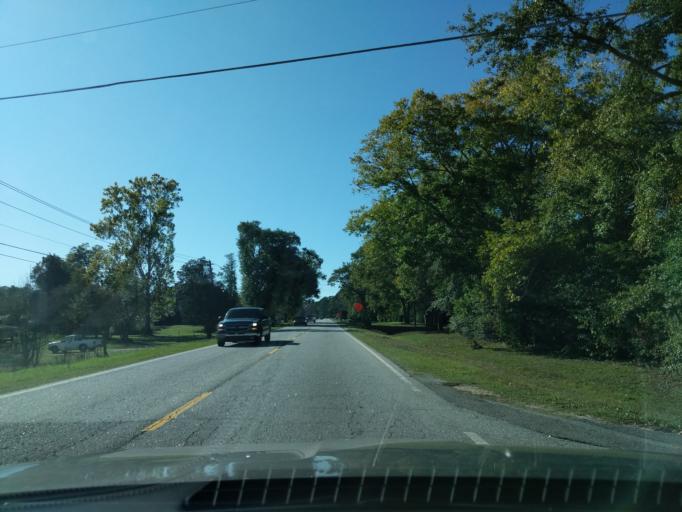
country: US
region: Georgia
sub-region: Columbia County
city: Grovetown
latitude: 33.4656
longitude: -82.1684
